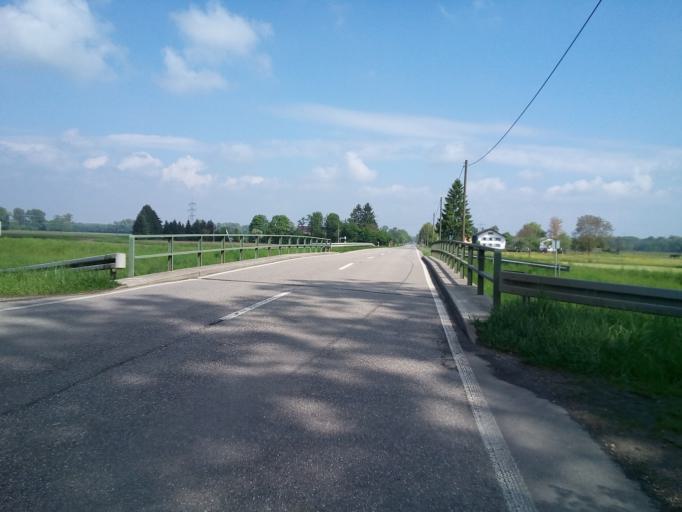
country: DE
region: Baden-Wuerttemberg
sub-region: Freiburg Region
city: Rheinau
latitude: 48.6533
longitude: 7.9926
